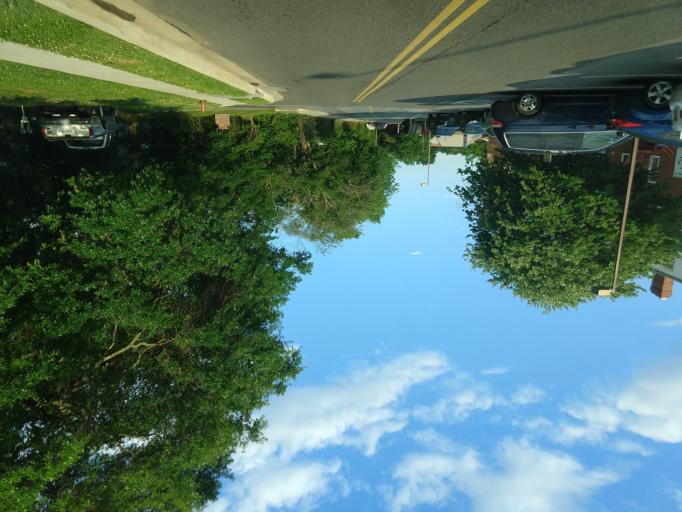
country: US
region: Maryland
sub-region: Prince George's County
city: College Park
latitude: 38.9830
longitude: -76.9356
